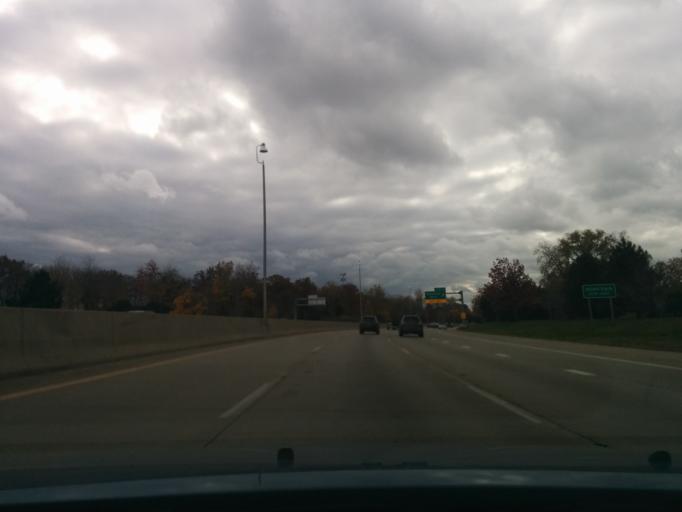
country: US
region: Michigan
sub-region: Wayne County
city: Melvindale
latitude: 42.2942
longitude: -83.2045
